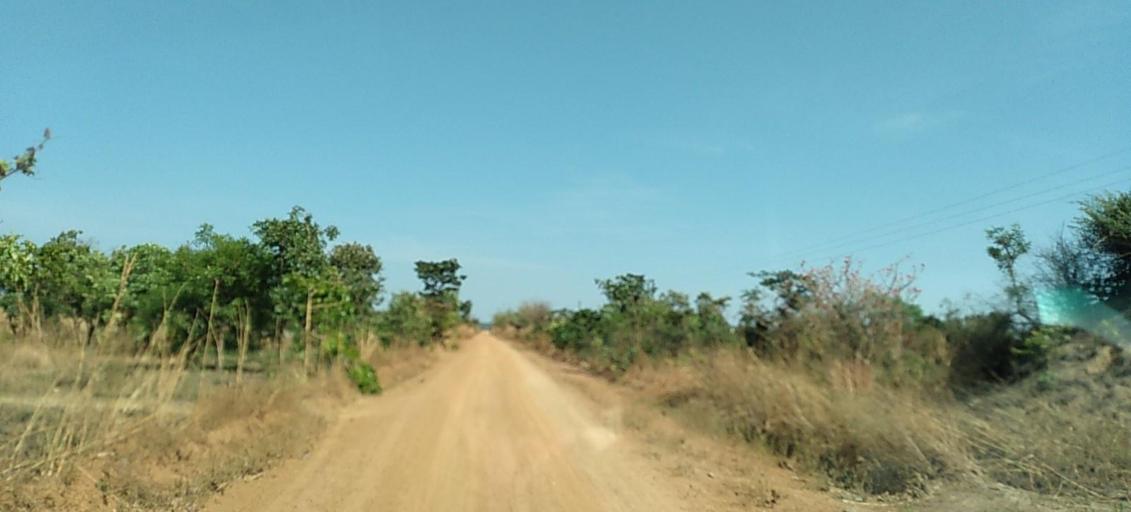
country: ZM
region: Copperbelt
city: Chililabombwe
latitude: -12.3457
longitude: 27.8757
